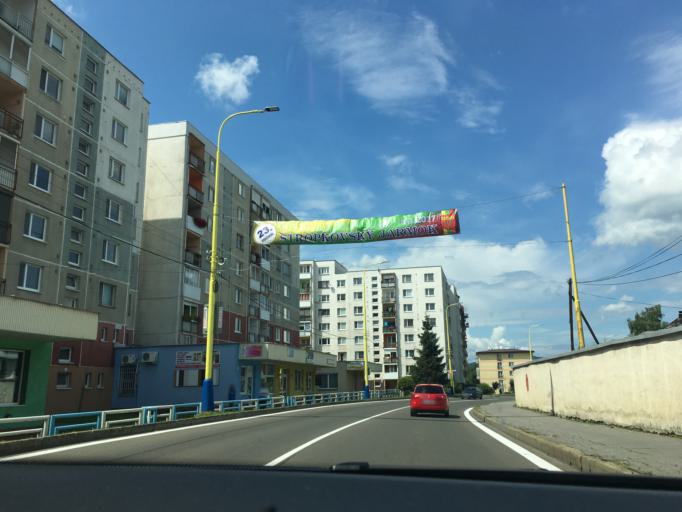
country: SK
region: Presovsky
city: Stropkov
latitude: 49.2048
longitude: 21.6507
